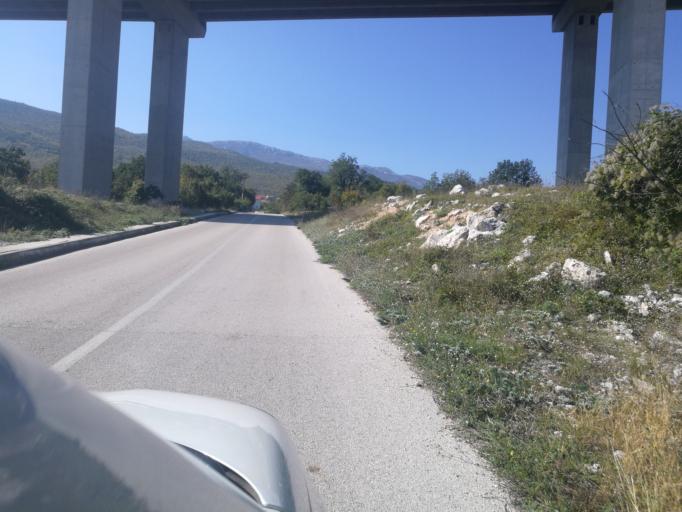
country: HR
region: Splitsko-Dalmatinska
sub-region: Grad Omis
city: Omis
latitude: 43.5175
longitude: 16.7390
